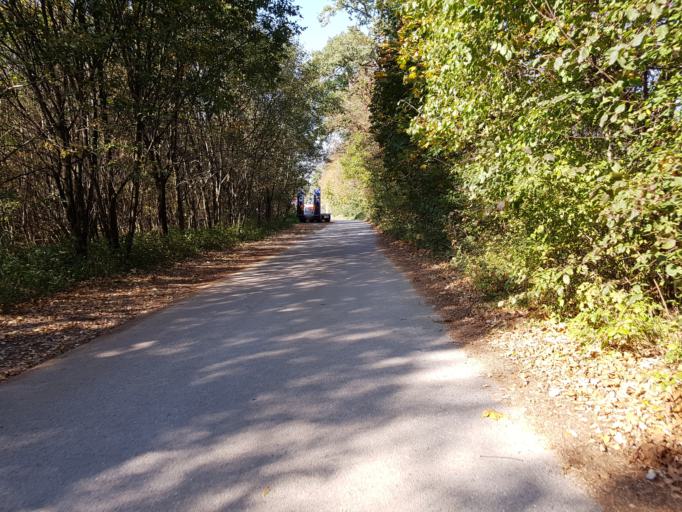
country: AT
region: Salzburg
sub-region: Politischer Bezirk Salzburg-Umgebung
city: Anif
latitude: 47.7369
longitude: 13.0715
